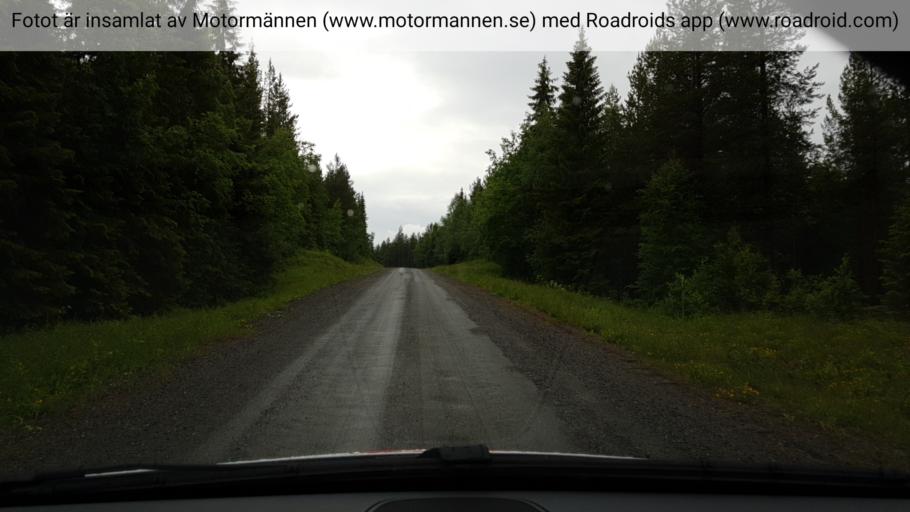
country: SE
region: Jaemtland
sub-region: Stroemsunds Kommun
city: Stroemsund
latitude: 64.2642
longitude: 15.0155
